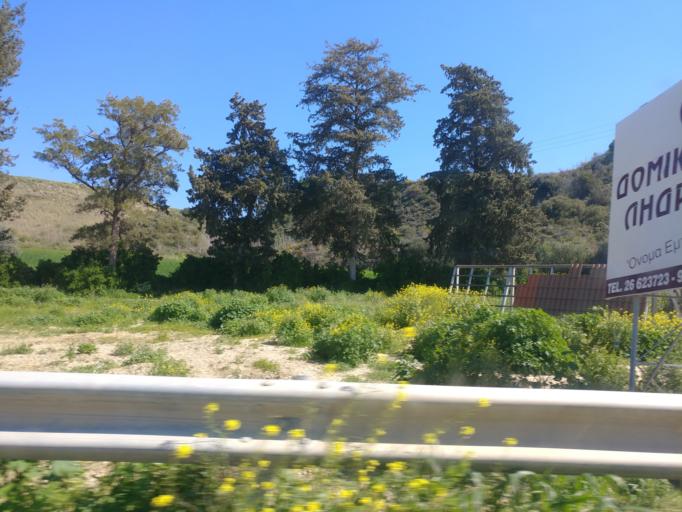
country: CY
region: Pafos
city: Polis
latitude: 35.0099
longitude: 32.4369
